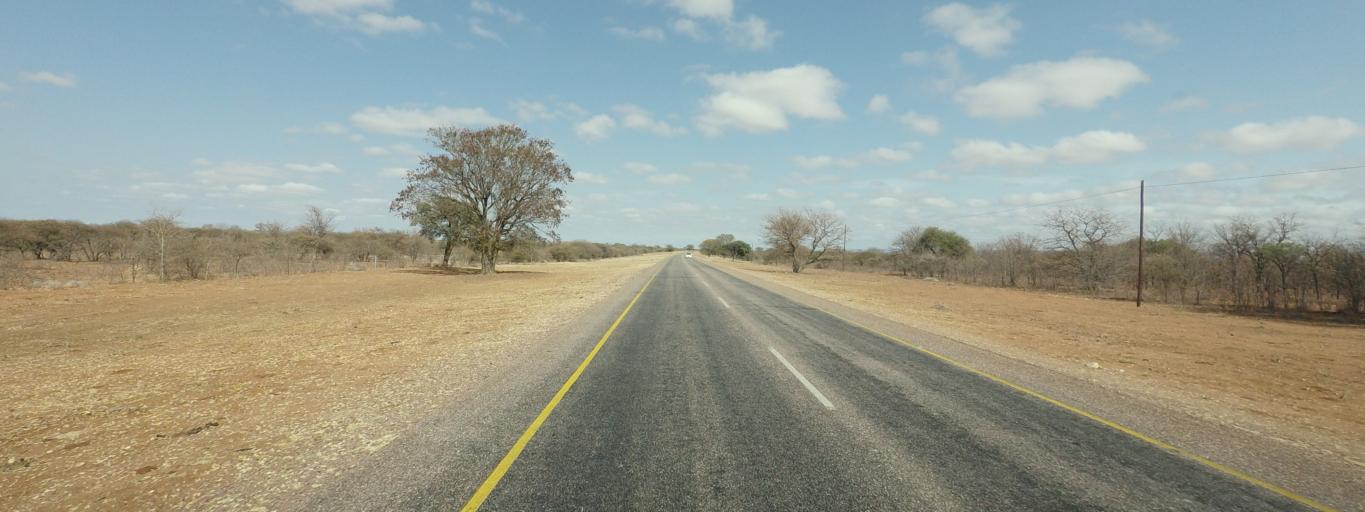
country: BW
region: Central
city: Ratholo
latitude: -22.8126
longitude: 27.5432
